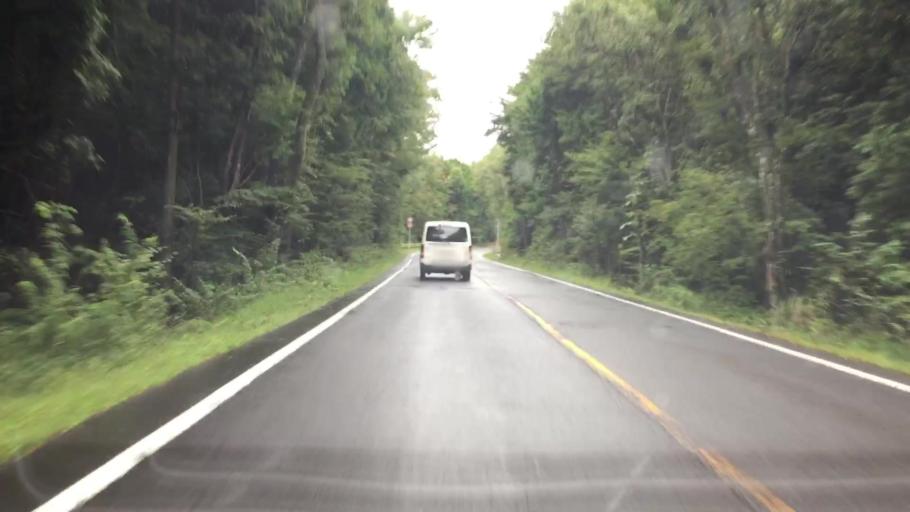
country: JP
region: Yamanashi
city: Fujikawaguchiko
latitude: 35.4687
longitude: 138.6670
